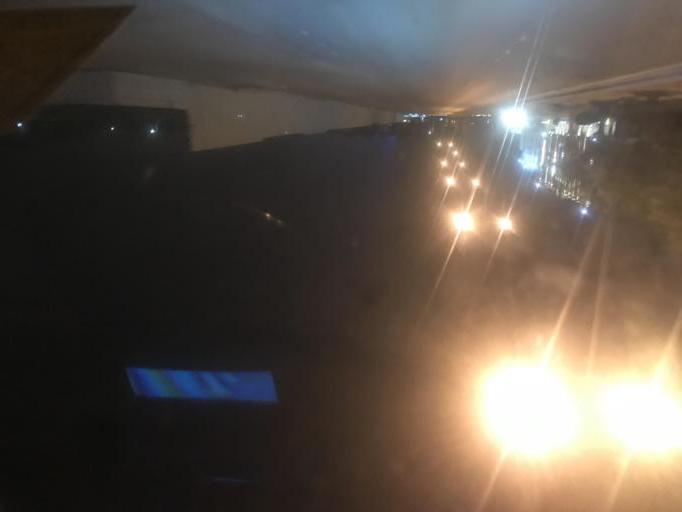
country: SA
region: Ar Riyad
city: Riyadh
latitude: 24.8009
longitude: 46.5932
